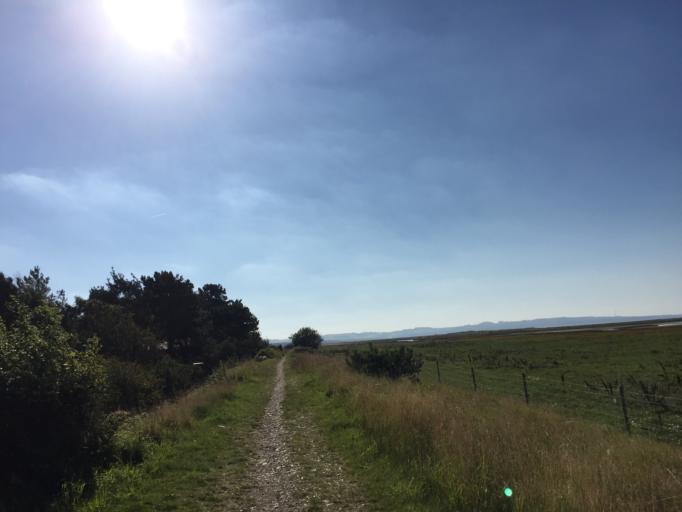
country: DK
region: Zealand
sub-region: Odsherred Kommune
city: Hojby
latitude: 55.8897
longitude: 11.5341
